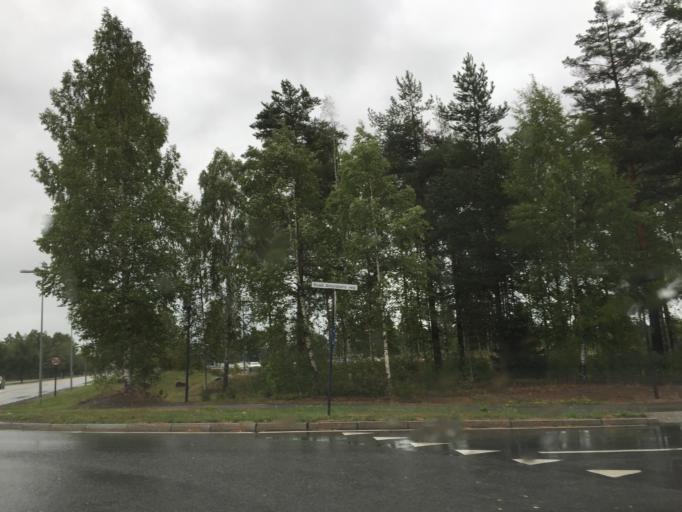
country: NO
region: Akershus
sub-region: Nannestad
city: Teigebyen
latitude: 60.1855
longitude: 11.0894
